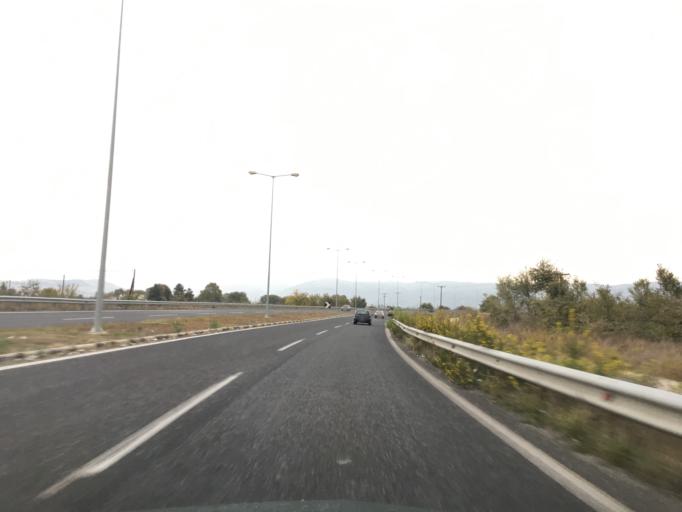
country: GR
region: Thessaly
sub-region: Trikala
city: Trikala
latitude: 39.5633
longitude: 21.8028
